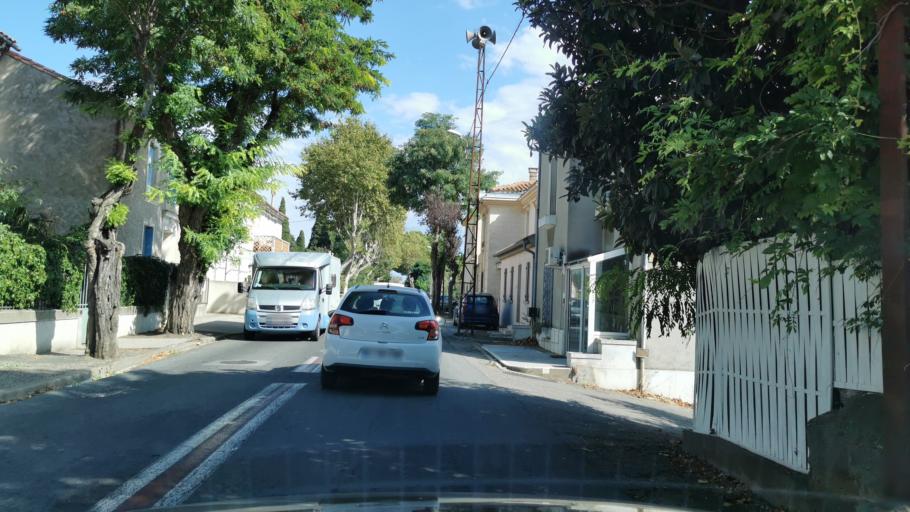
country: FR
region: Languedoc-Roussillon
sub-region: Departement de l'Aude
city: Azille
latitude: 43.2503
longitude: 2.6578
